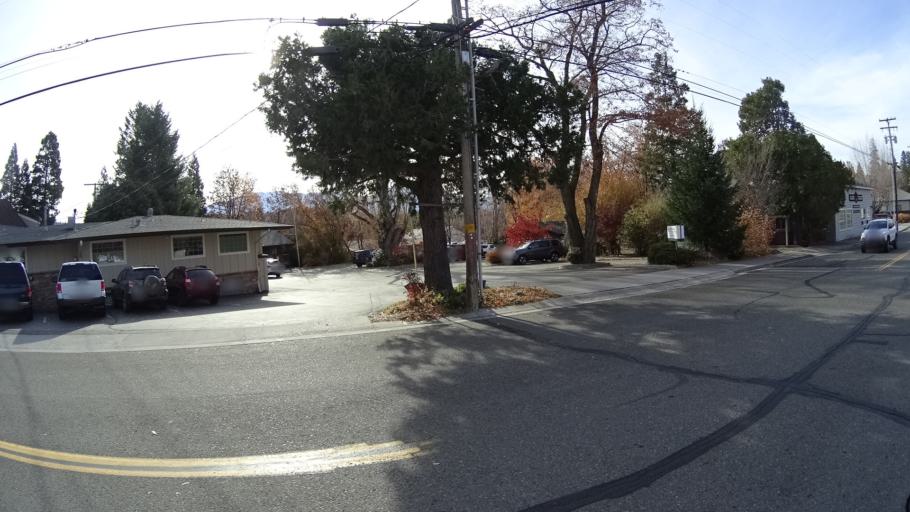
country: US
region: California
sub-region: Siskiyou County
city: Weed
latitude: 41.4271
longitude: -122.3849
